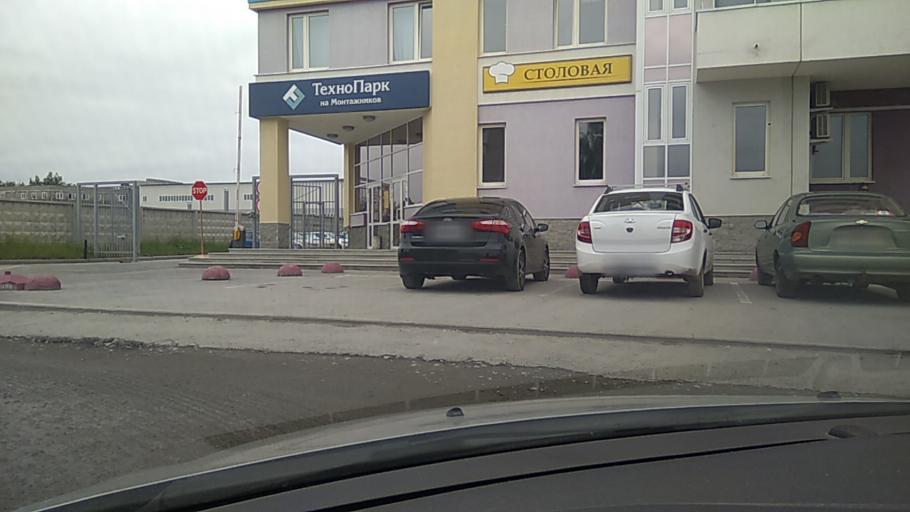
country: RU
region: Sverdlovsk
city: Shuvakish
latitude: 56.8945
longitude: 60.5183
